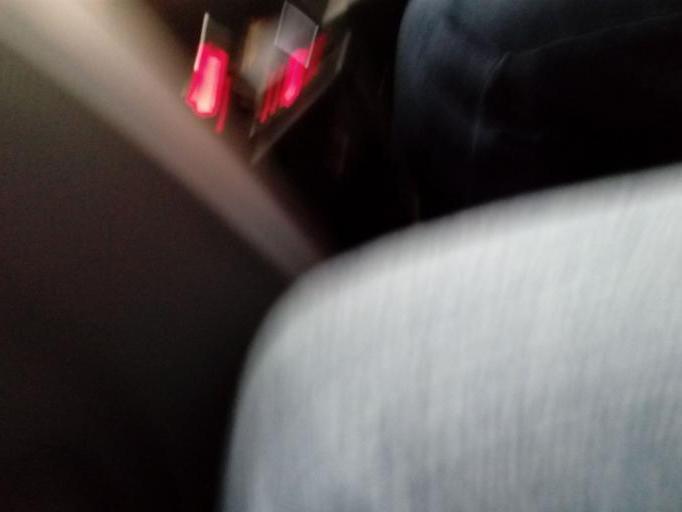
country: LK
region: Western
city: Moratuwa
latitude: 6.7954
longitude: 79.8996
